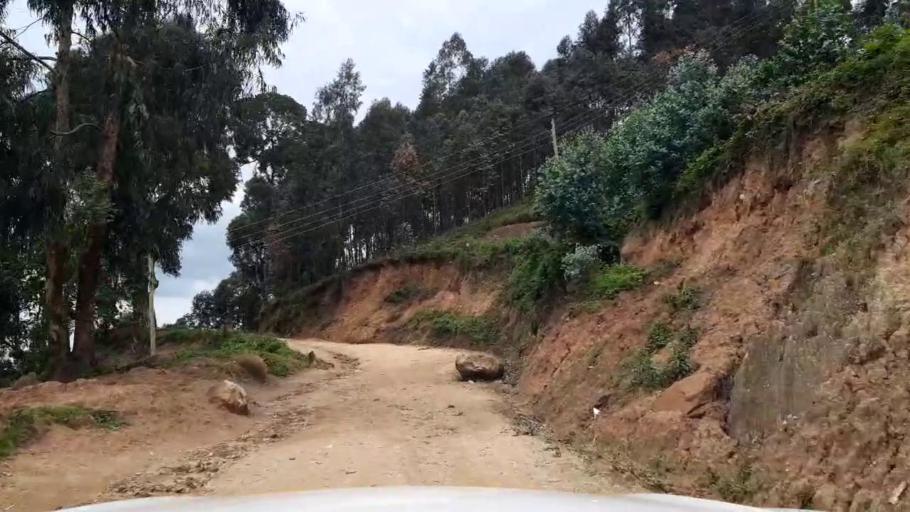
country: RW
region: Western Province
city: Kibuye
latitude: -1.9661
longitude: 29.3950
